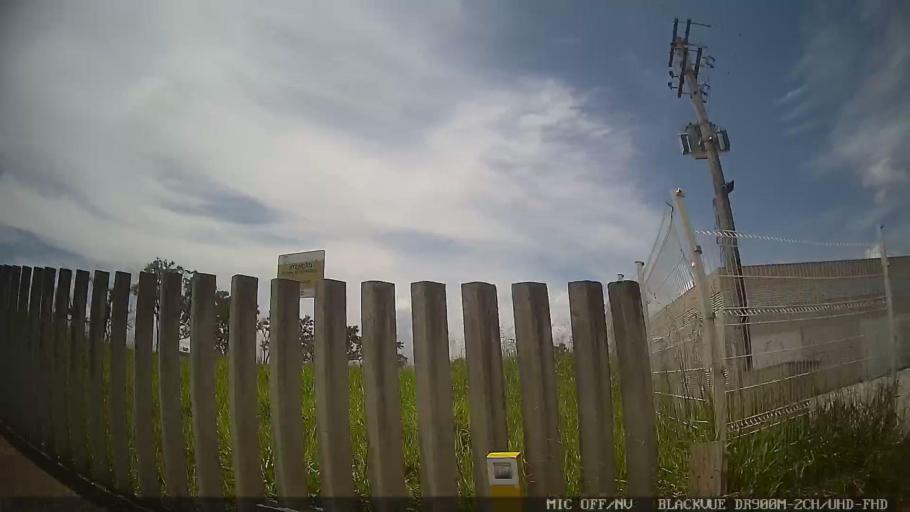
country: BR
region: Sao Paulo
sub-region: Jarinu
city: Jarinu
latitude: -23.0649
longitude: -46.6403
